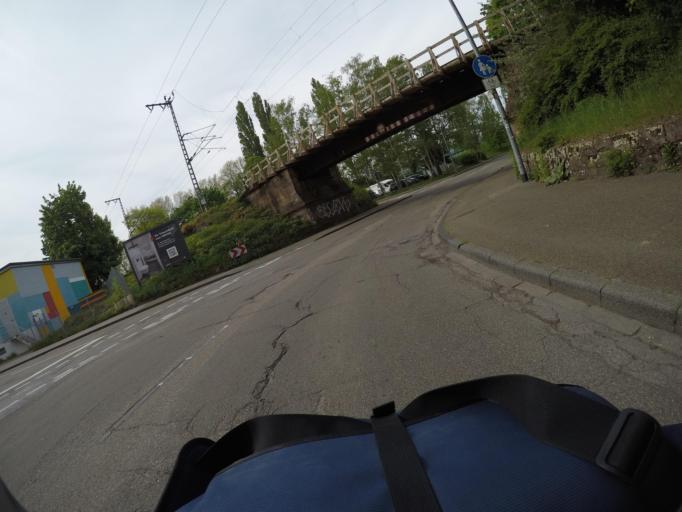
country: DE
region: Baden-Wuerttemberg
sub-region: Karlsruhe Region
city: Rastatt
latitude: 48.8581
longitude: 8.2152
